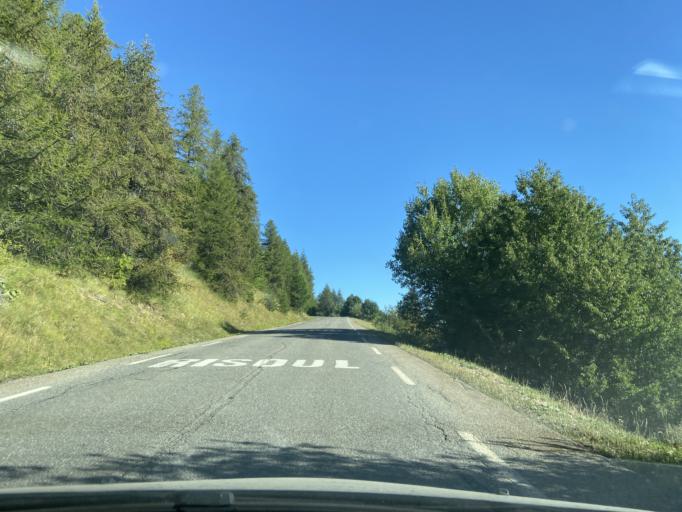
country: FR
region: Provence-Alpes-Cote d'Azur
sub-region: Departement des Hautes-Alpes
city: Guillestre
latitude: 44.6299
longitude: 6.6292
